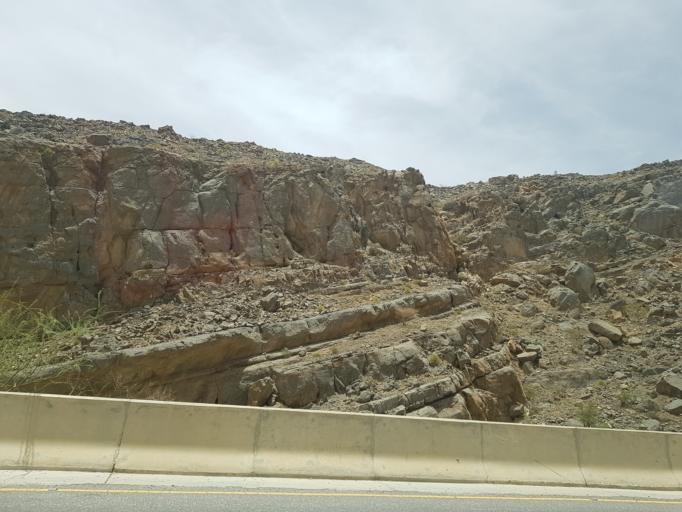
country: OM
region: Muhafazat ad Dakhiliyah
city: Izki
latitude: 22.9562
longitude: 57.6747
